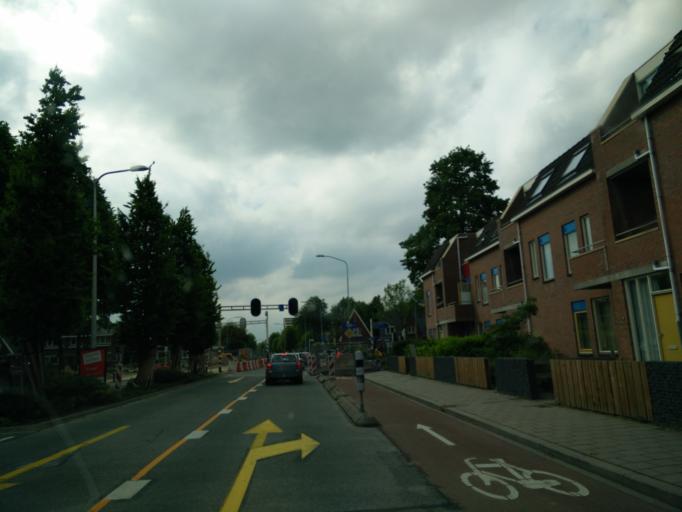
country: NL
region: Drenthe
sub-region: Gemeente Assen
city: Assen
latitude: 52.9965
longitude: 6.5565
